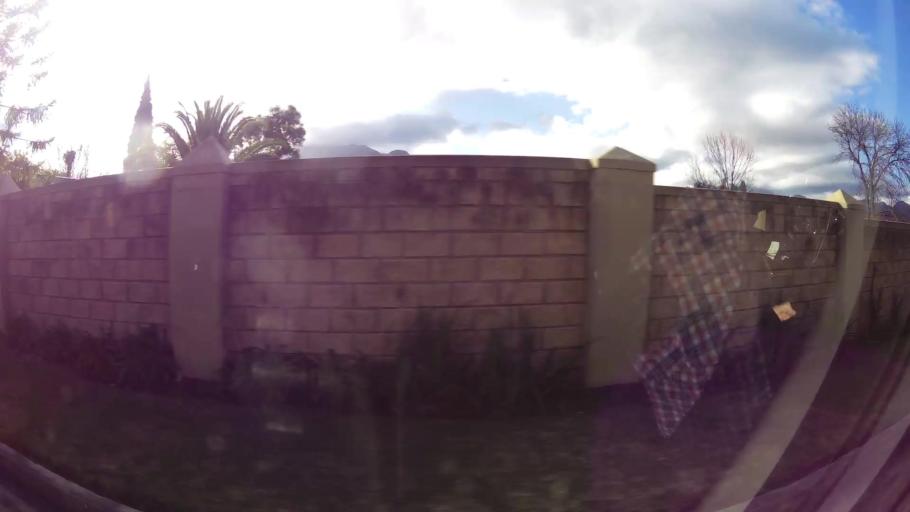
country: ZA
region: Western Cape
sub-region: Eden District Municipality
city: George
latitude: -33.9546
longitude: 22.4728
